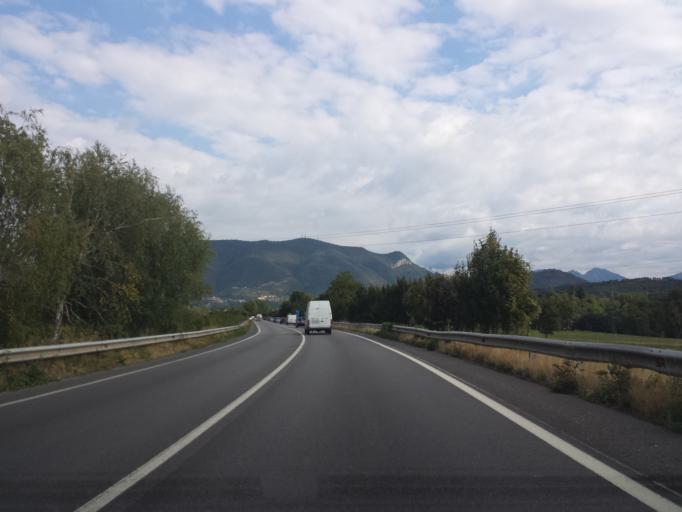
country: IT
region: Lombardy
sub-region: Provincia di Brescia
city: Muscoline
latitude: 45.5650
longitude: 10.4419
